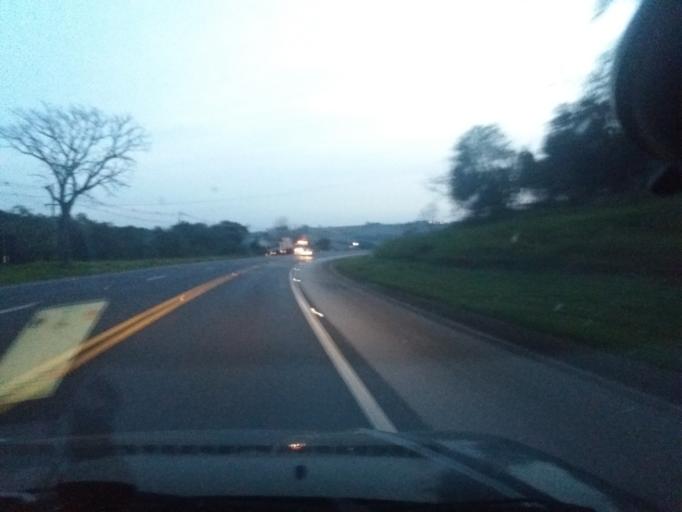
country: BR
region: Sao Paulo
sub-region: Itapeva
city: Itapeva
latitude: -23.9781
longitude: -48.8327
